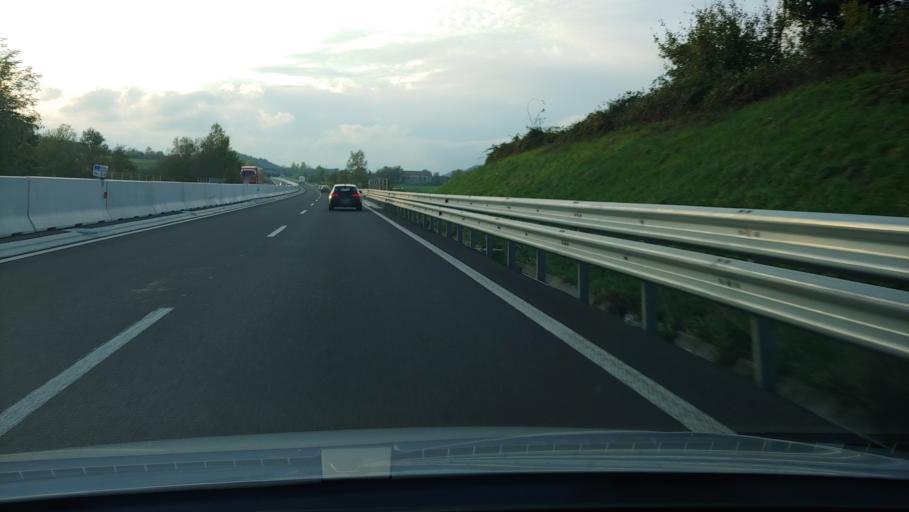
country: SI
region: Ajdovscina
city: Lokavec
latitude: 45.8847
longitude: 13.8773
